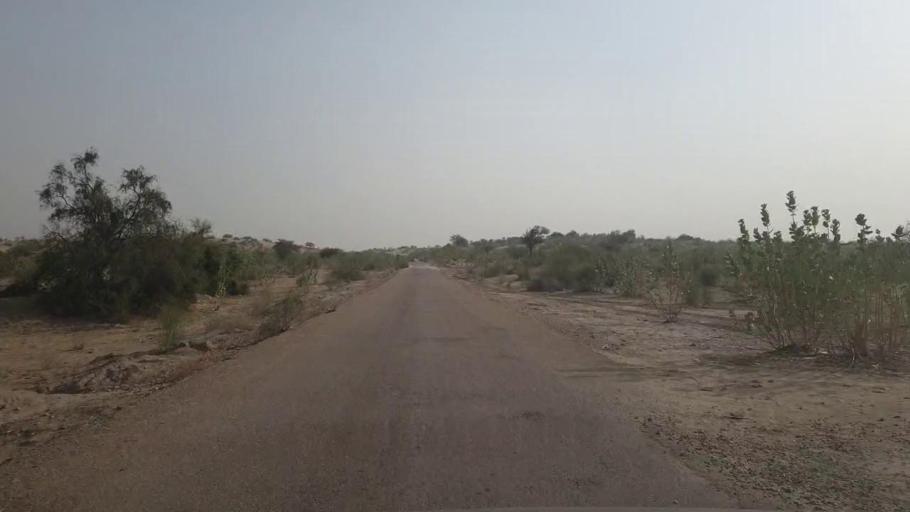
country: PK
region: Sindh
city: Chor
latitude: 25.5340
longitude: 69.9602
